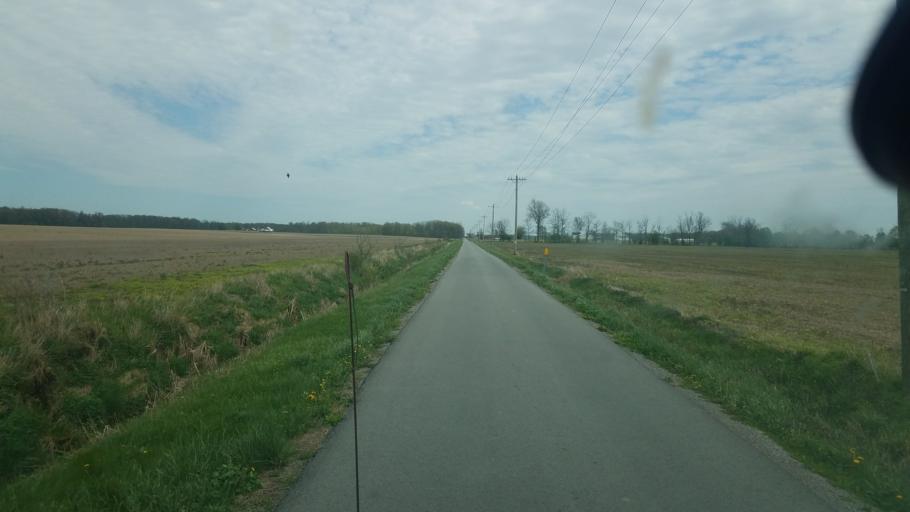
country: US
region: Ohio
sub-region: Hancock County
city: Arlington
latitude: 40.8489
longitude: -83.7469
